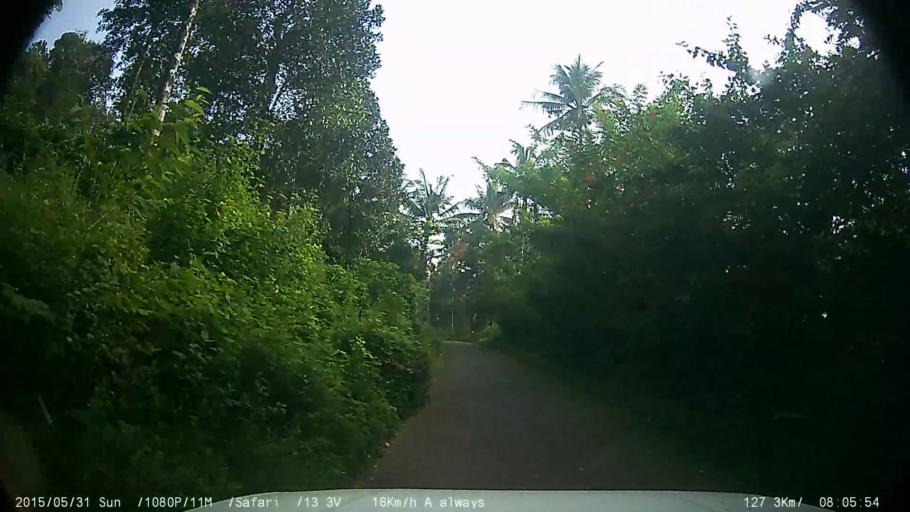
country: IN
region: Kerala
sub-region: Wayanad
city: Kalpetta
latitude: 11.6354
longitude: 76.0328
